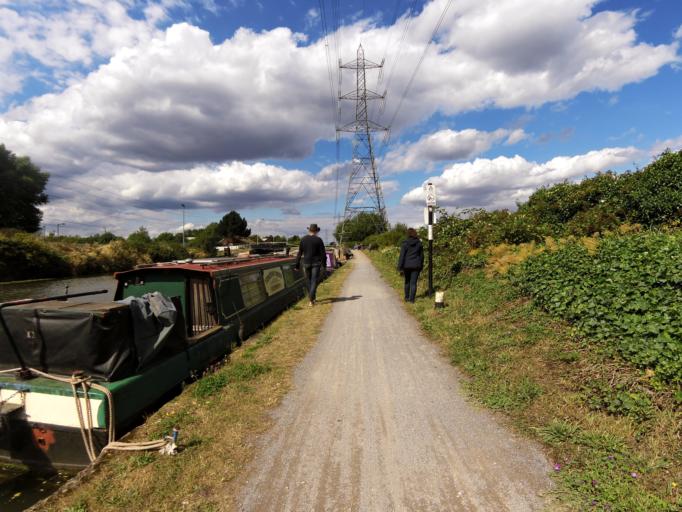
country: GB
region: England
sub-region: Greater London
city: Walthamstow
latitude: 51.6252
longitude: -0.0326
